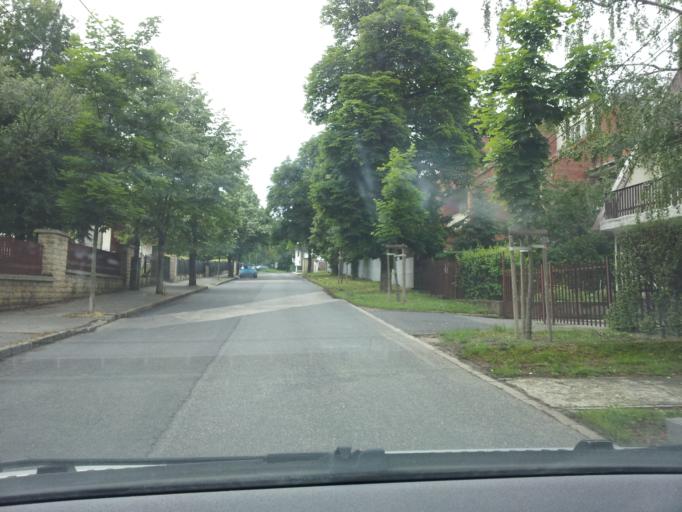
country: HU
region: Budapest
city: Budapest XII. keruelet
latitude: 47.5173
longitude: 18.9844
